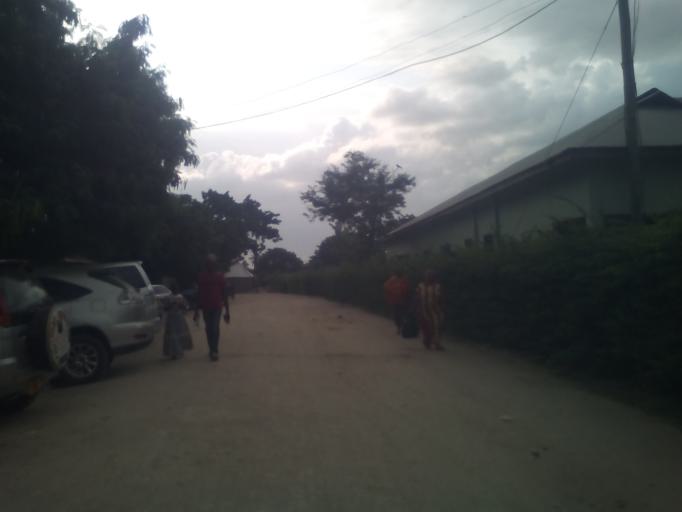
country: TZ
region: Dar es Salaam
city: Dar es Salaam
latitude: -6.8418
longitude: 39.2762
